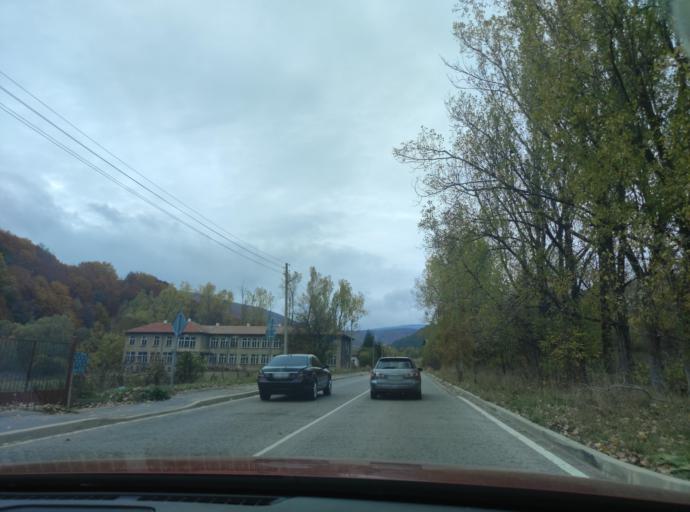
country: BG
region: Sofiya
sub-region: Obshtina Godech
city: Godech
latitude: 43.0794
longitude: 23.1068
